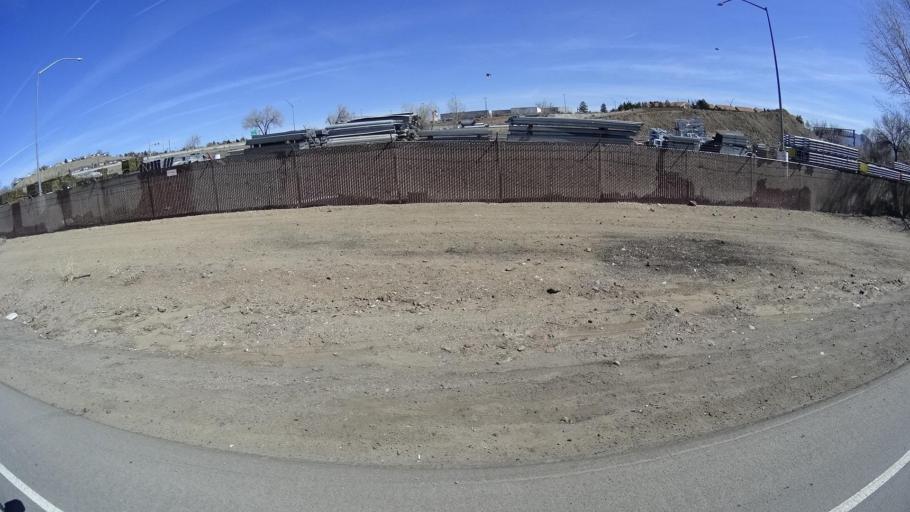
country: US
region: Nevada
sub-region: Washoe County
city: Reno
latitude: 39.5538
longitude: -119.7911
